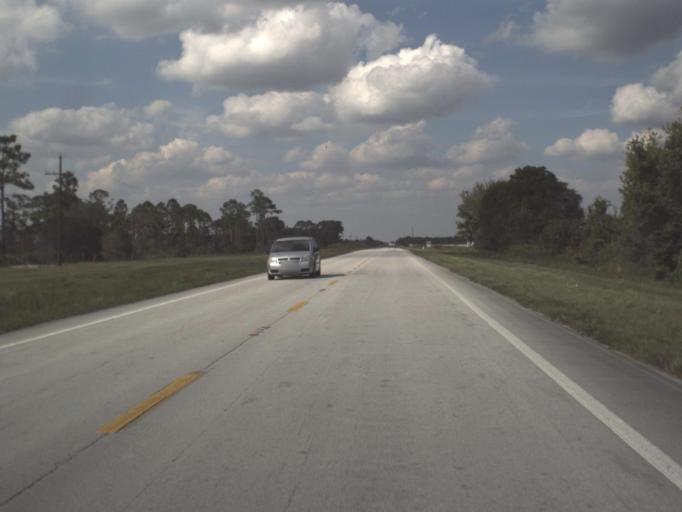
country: US
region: Florida
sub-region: Indian River County
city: Fellsmere
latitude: 27.5916
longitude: -80.8425
